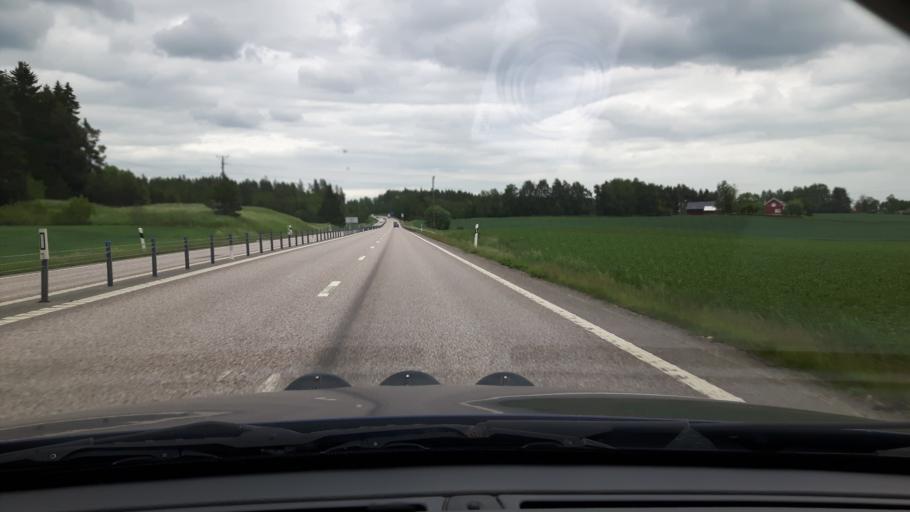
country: SE
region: Soedermanland
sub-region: Katrineholms Kommun
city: Katrineholm
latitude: 59.0212
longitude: 16.3440
